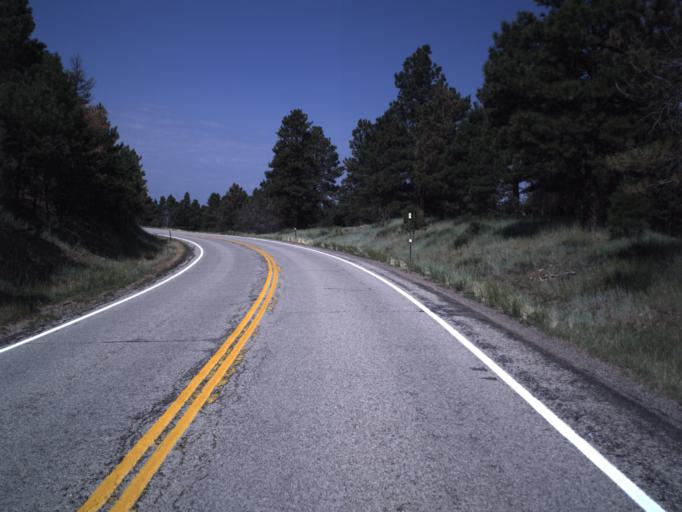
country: US
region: Utah
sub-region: Daggett County
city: Manila
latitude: 40.8704
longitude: -109.5058
